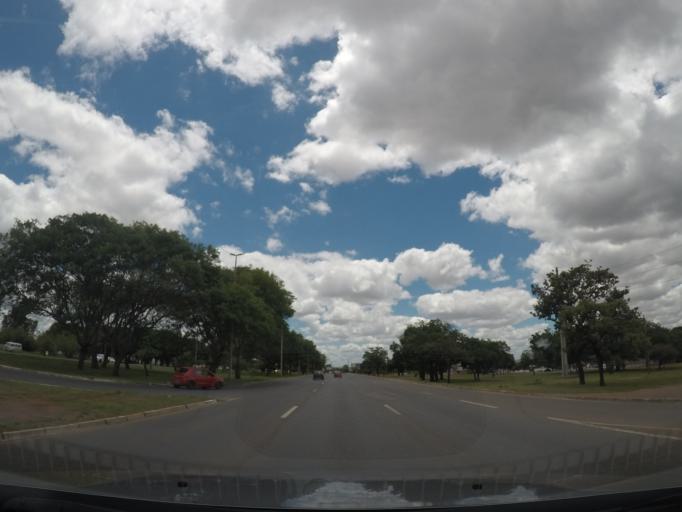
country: BR
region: Federal District
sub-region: Brasilia
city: Brasilia
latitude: -15.7677
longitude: -47.9344
